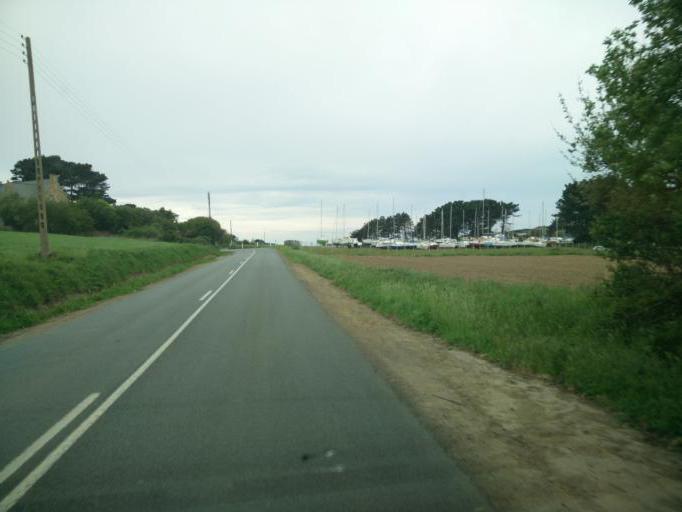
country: FR
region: Brittany
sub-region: Departement des Cotes-d'Armor
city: Trebeurden
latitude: 48.7884
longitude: -3.5740
